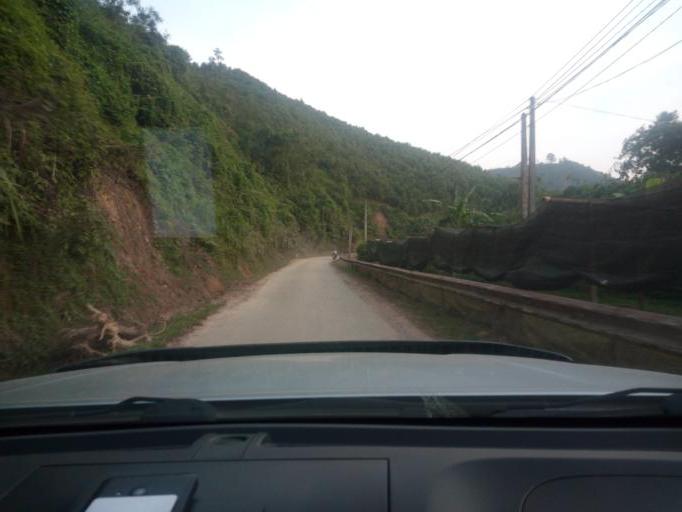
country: VN
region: Yen Bai
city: Co Phuc
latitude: 21.8580
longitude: 104.6204
